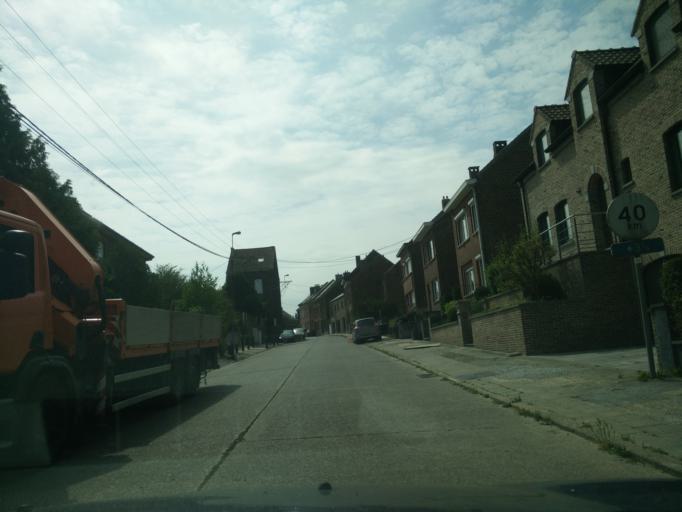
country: BE
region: Wallonia
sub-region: Province du Brabant Wallon
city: Tubize
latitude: 50.6919
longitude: 4.2217
